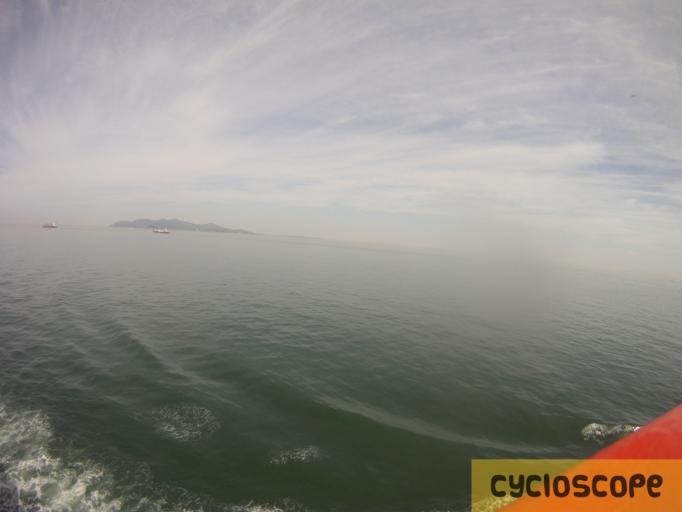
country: KR
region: Incheon
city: Incheon
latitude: 37.3429
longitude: 126.4967
